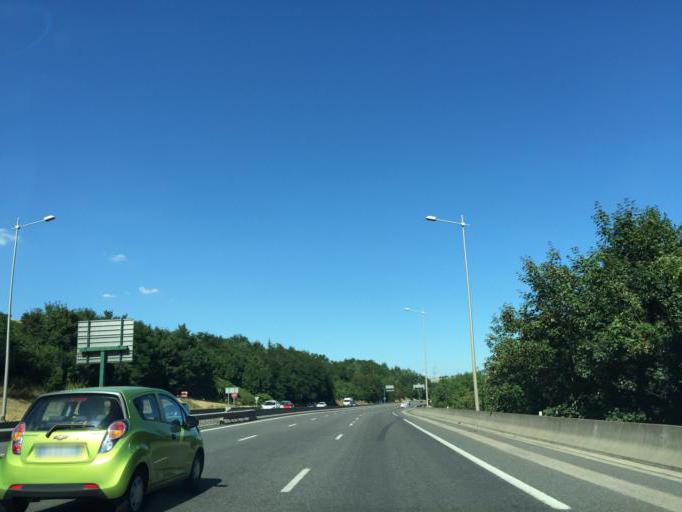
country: FR
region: Rhone-Alpes
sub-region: Departement de la Loire
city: Saint-Jean-Bonnefonds
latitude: 45.4398
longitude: 4.4552
